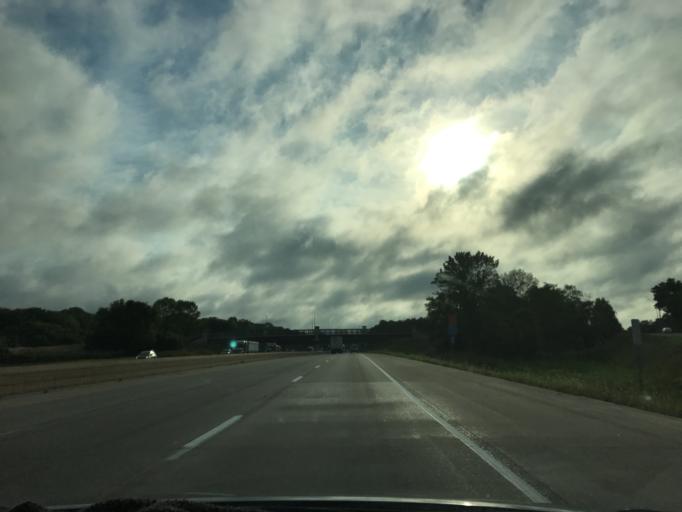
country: US
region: Iowa
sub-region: Johnson County
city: Iowa City
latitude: 41.6860
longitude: -91.5436
